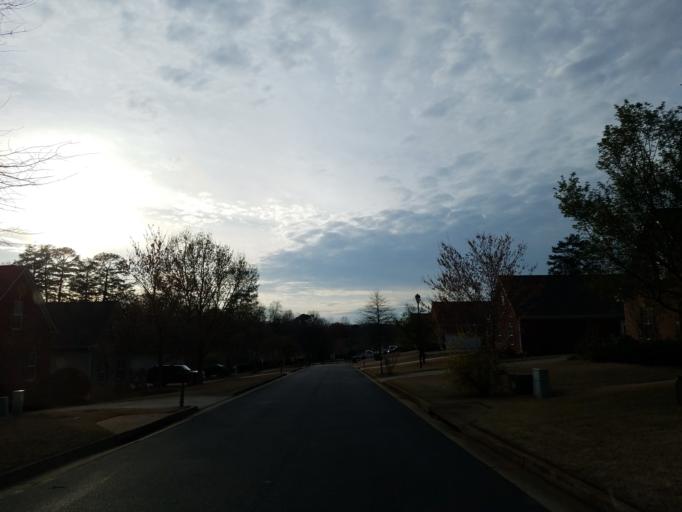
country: US
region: Georgia
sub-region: Dawson County
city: Dawsonville
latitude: 34.4272
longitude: -84.1226
